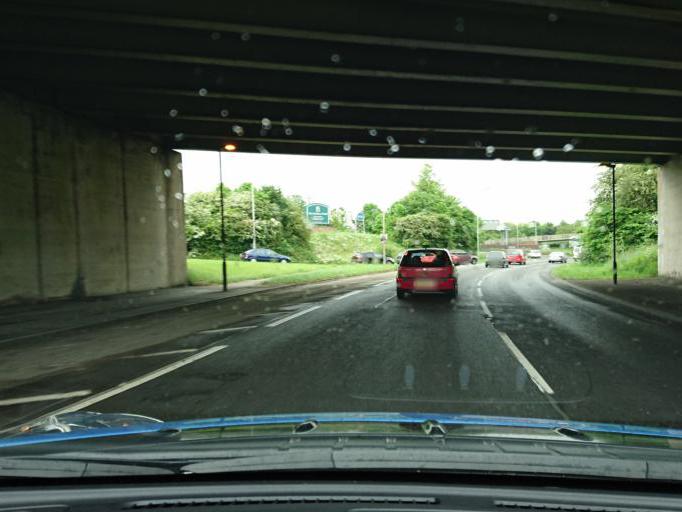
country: GB
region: England
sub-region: Borough of Swindon
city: Wanborough
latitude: 51.5770
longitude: -1.7342
